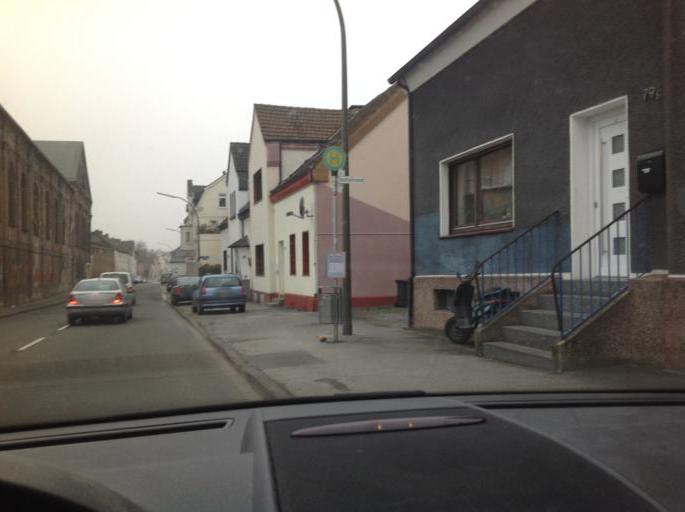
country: DE
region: North Rhine-Westphalia
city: Witten
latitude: 51.5017
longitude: 7.3717
